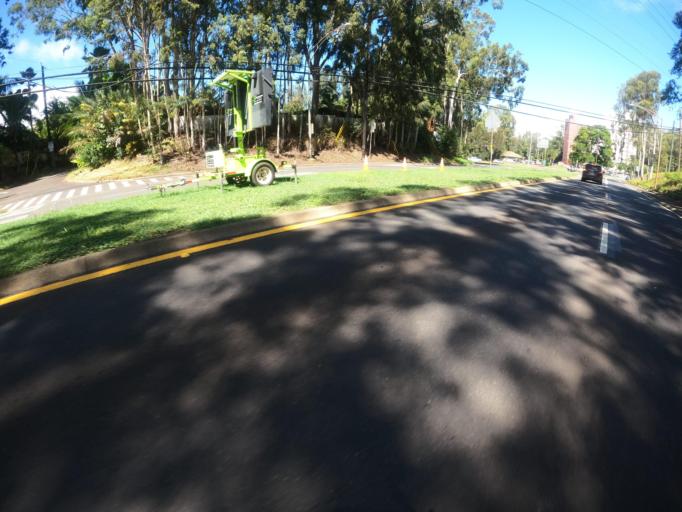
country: US
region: Hawaii
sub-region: Honolulu County
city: Wahiawa
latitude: 21.4878
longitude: -158.0402
